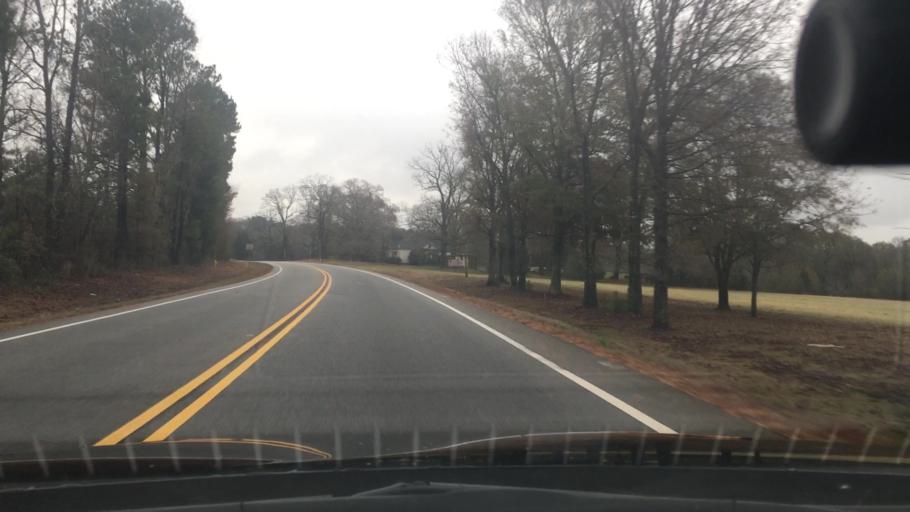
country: US
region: Georgia
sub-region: Spalding County
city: Experiment
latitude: 33.2411
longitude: -84.4235
